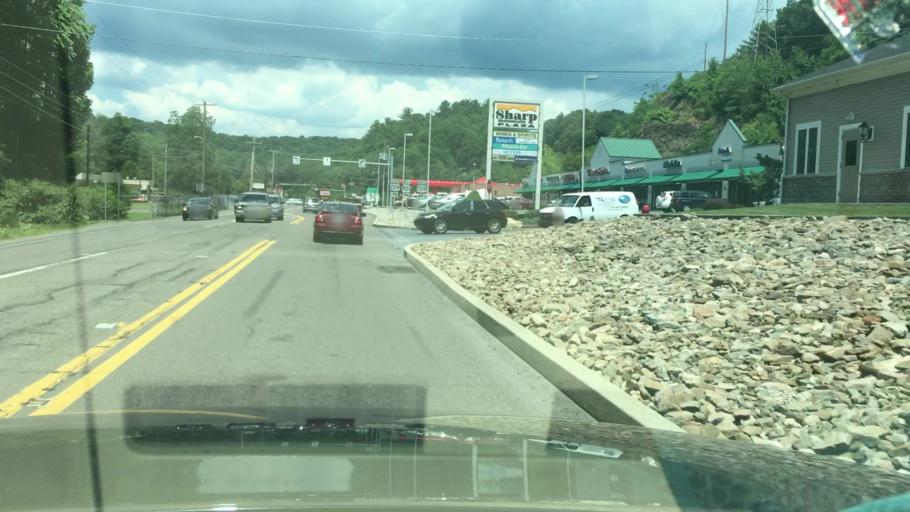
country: US
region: Pennsylvania
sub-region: Schuylkill County
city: Minersville
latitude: 40.6705
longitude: -76.2355
